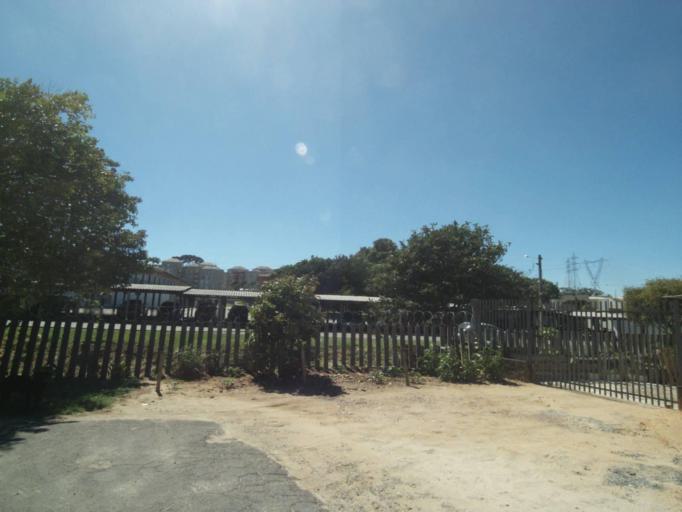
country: BR
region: Parana
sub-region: Curitiba
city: Curitiba
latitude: -25.4867
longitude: -49.3430
